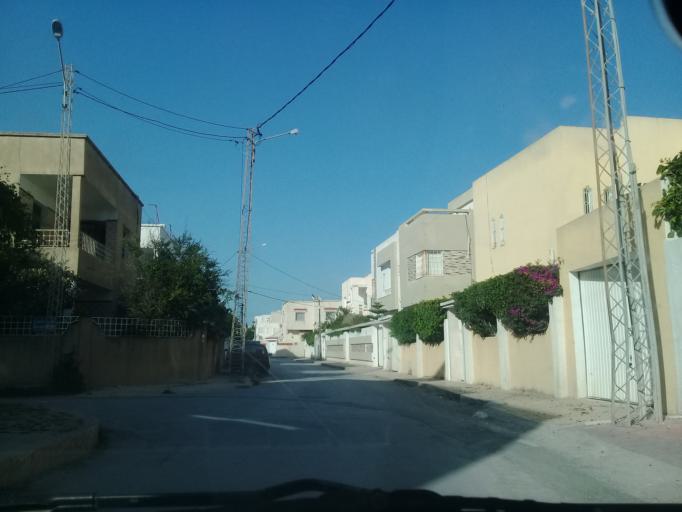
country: TN
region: Ariana
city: Ariana
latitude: 36.8350
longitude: 10.1948
